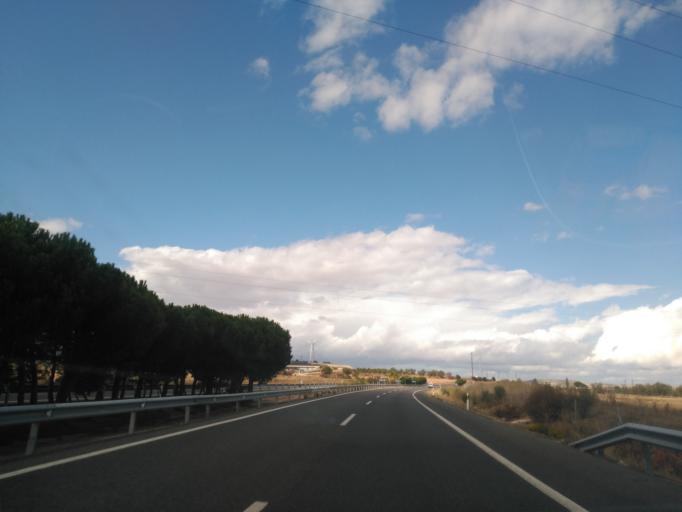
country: ES
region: Castille and Leon
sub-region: Provincia de Burgos
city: Villaquiran de los Infantes
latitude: 42.2169
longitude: -4.0056
